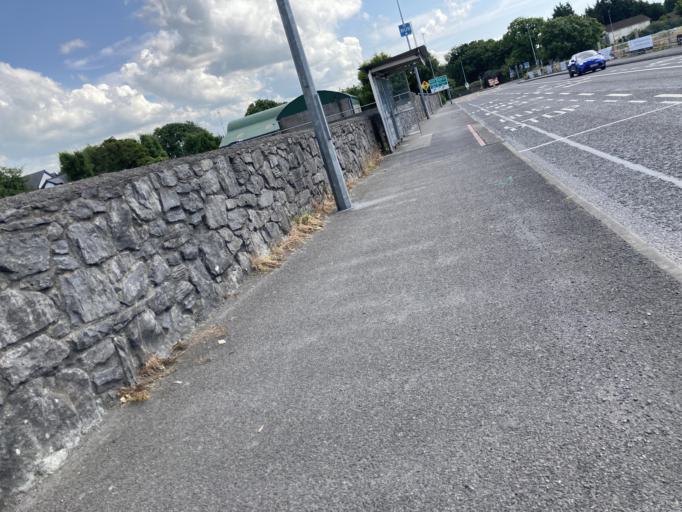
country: IE
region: Connaught
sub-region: County Galway
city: Claregalway
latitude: 53.2936
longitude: -8.9842
